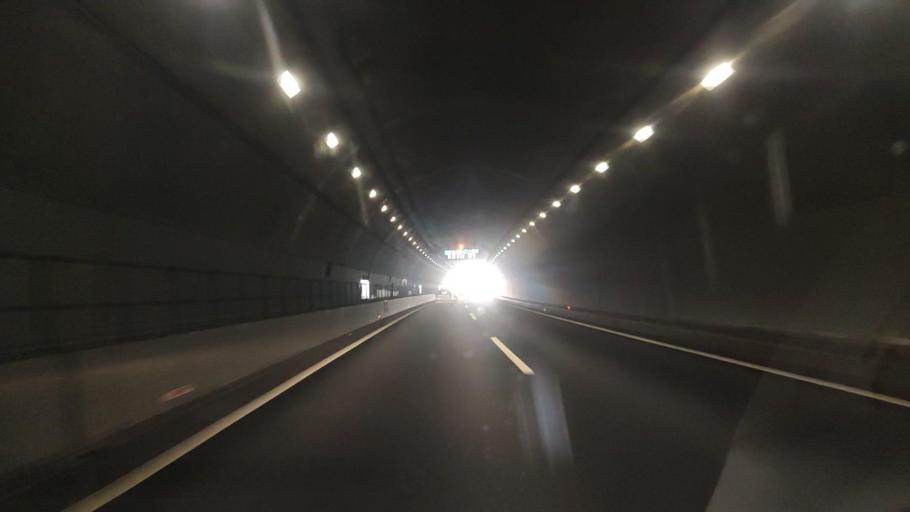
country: JP
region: Kanagawa
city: Zama
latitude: 35.5262
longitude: 139.3487
